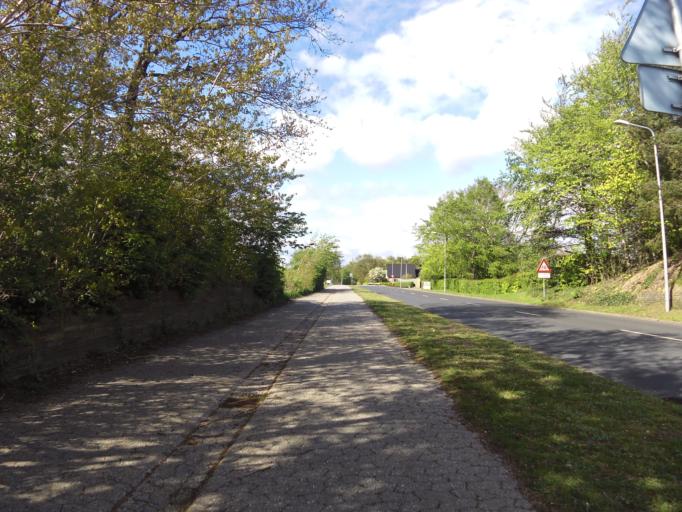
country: DK
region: South Denmark
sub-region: Esbjerg Kommune
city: Ribe
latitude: 55.2826
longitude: 8.7256
